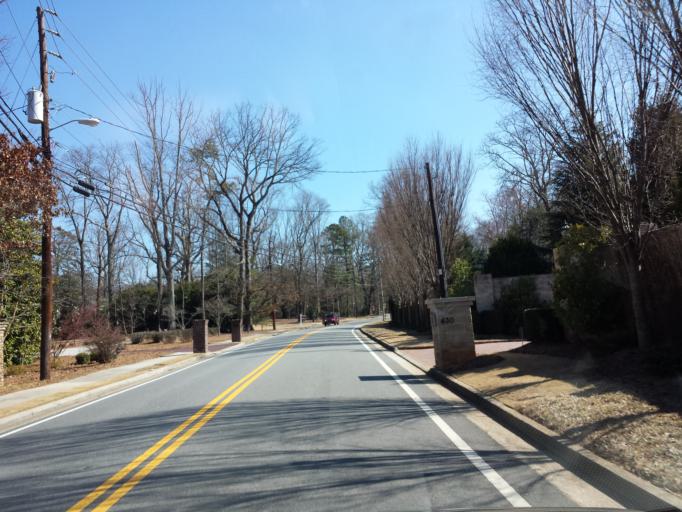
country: US
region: Georgia
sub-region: Fulton County
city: Sandy Springs
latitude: 33.9185
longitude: -84.4012
